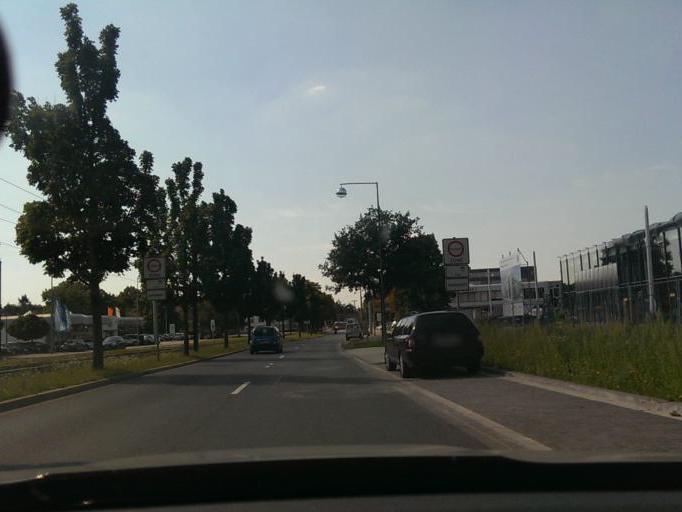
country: DE
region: Lower Saxony
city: Hannover
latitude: 52.4043
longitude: 9.7951
